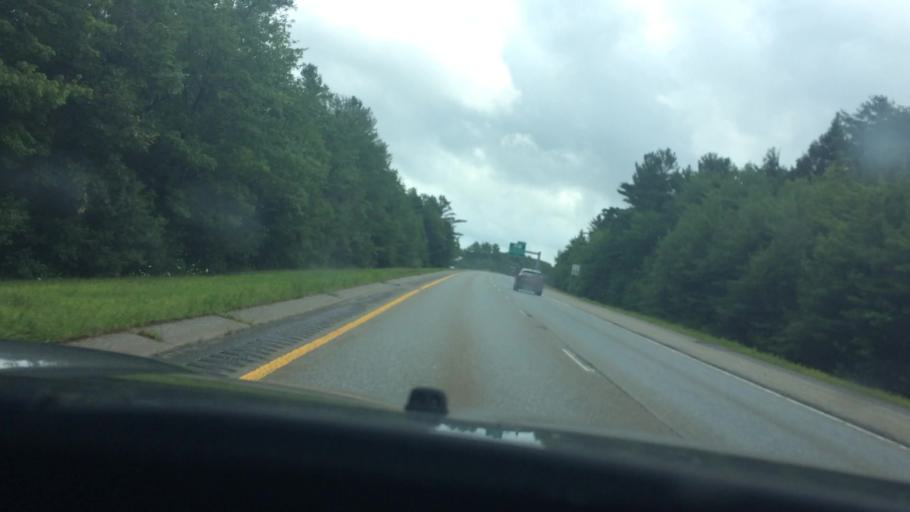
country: US
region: Massachusetts
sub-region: Worcester County
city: Templeton
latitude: 42.5673
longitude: -72.0641
